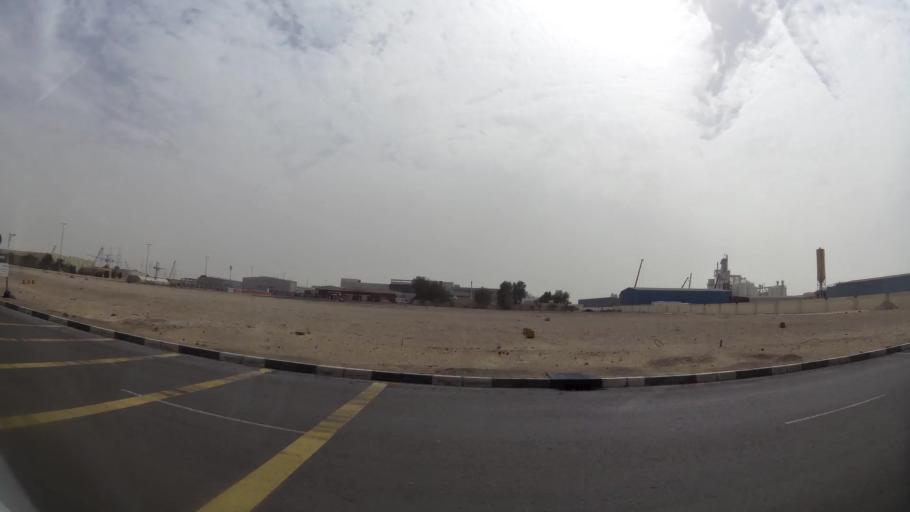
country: AE
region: Abu Dhabi
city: Abu Dhabi
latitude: 24.3233
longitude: 54.5035
